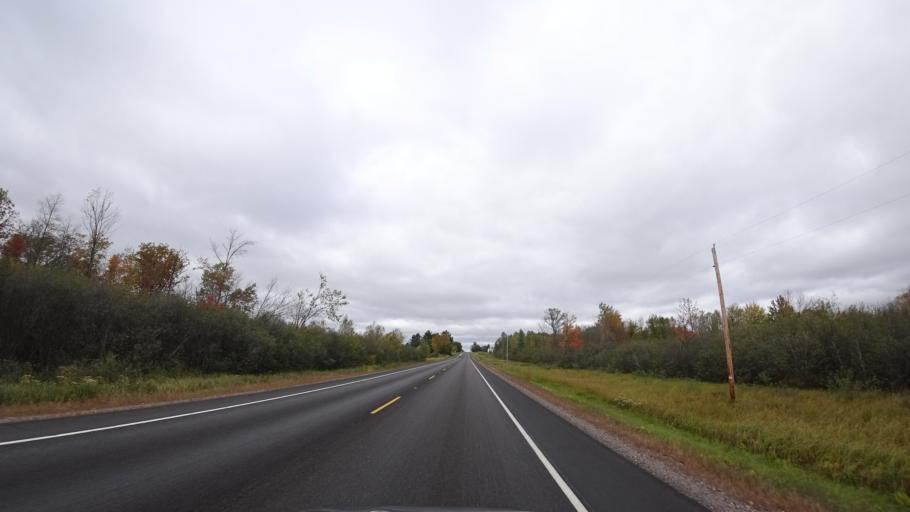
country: US
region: Wisconsin
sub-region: Rusk County
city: Ladysmith
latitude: 45.3566
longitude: -91.1108
